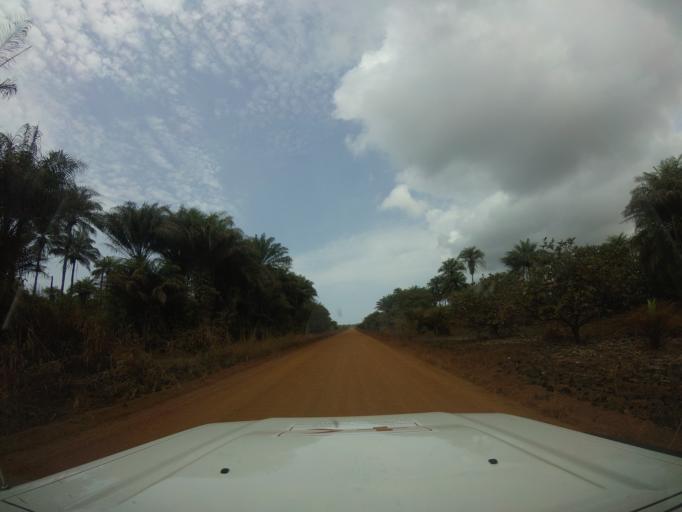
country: LR
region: Grand Cape Mount
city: Robertsport
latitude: 6.7033
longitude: -11.3112
